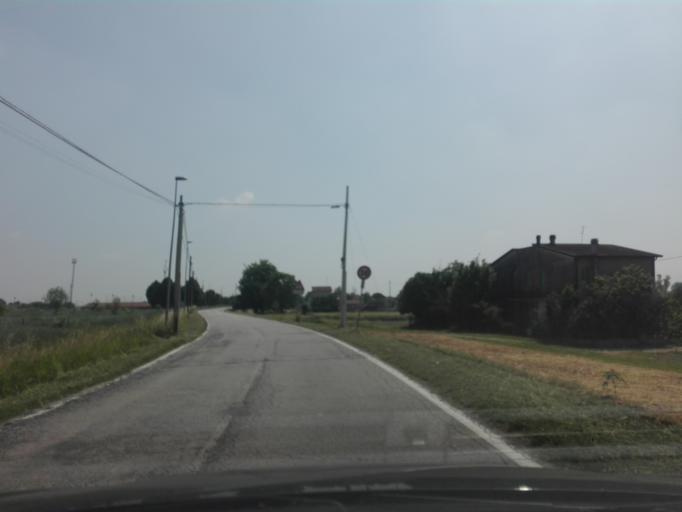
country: IT
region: Veneto
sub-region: Provincia di Rovigo
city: Ceregnano
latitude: 45.0455
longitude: 11.8861
